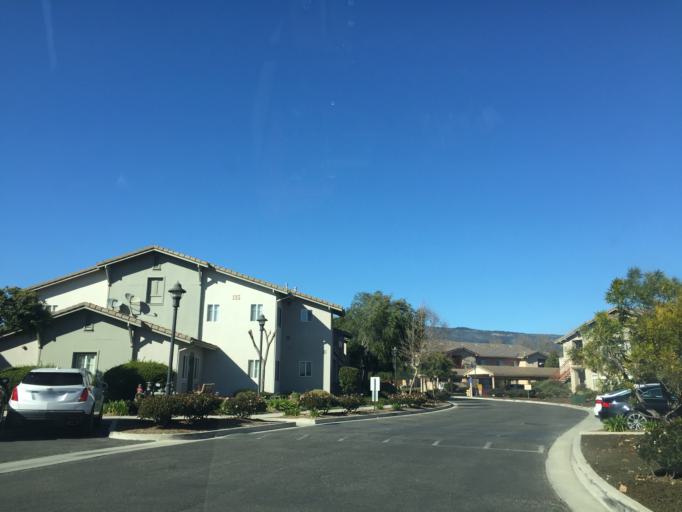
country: US
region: California
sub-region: Santa Barbara County
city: Isla Vista
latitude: 34.4321
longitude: -119.8504
